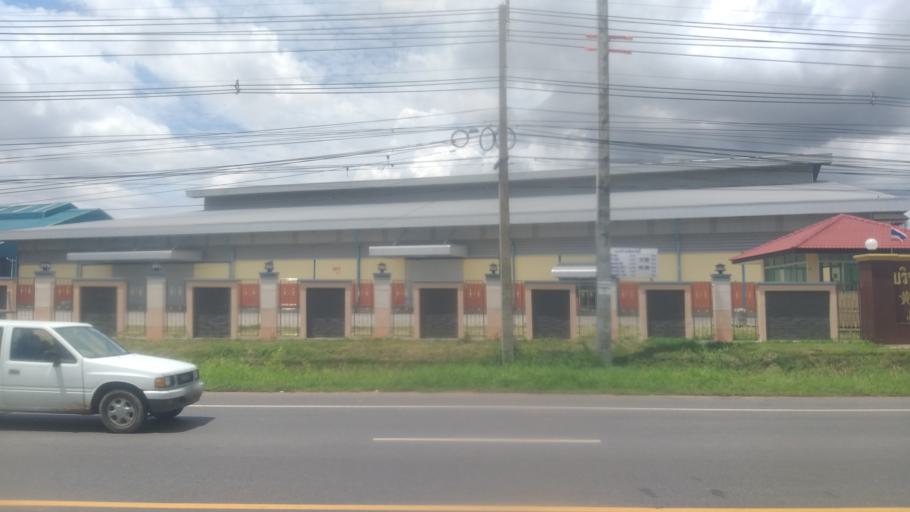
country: TH
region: Nakhon Ratchasima
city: Nakhon Ratchasima
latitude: 15.0857
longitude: 102.1122
